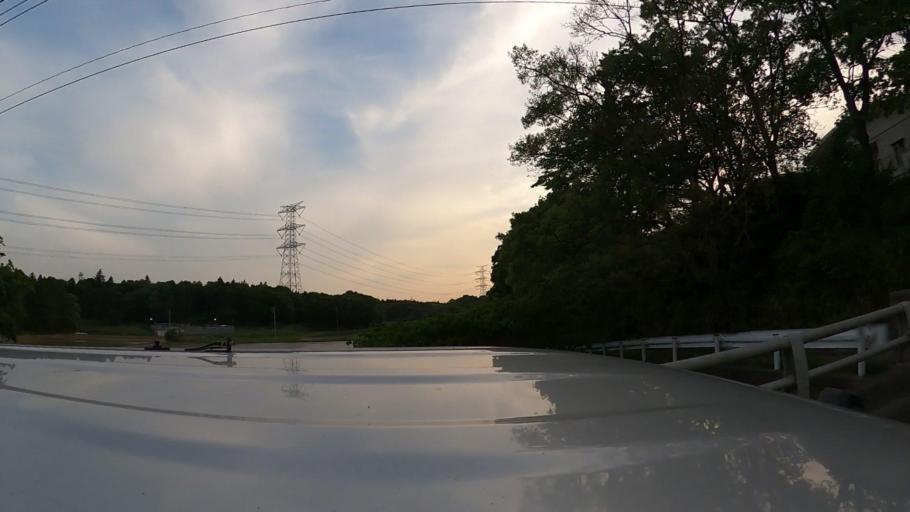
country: JP
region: Ibaraki
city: Ushiku
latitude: 36.0062
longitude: 140.1154
